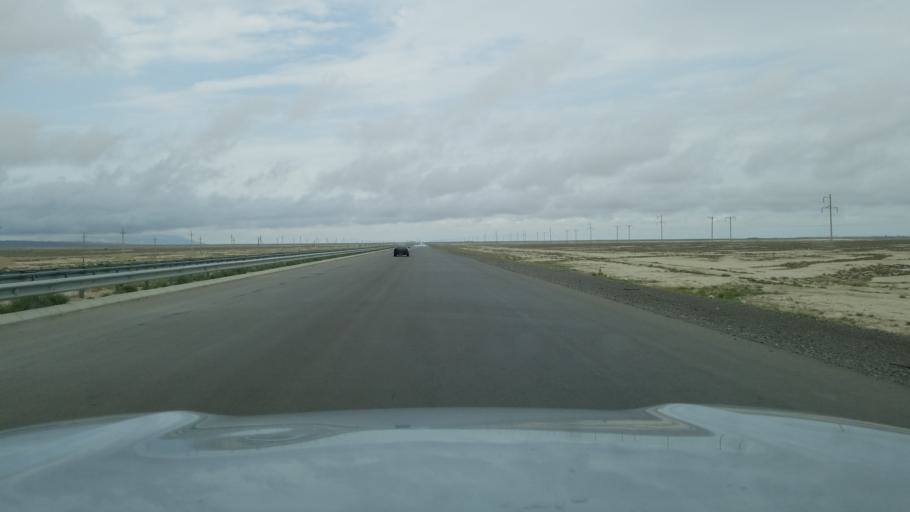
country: TM
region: Balkan
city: Serdar
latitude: 39.1175
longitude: 55.9122
